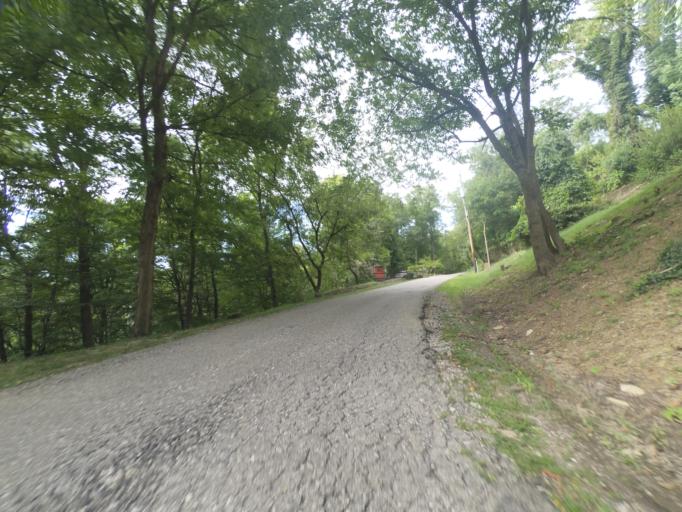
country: US
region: West Virginia
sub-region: Cabell County
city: Huntington
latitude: 38.4026
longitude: -82.4464
